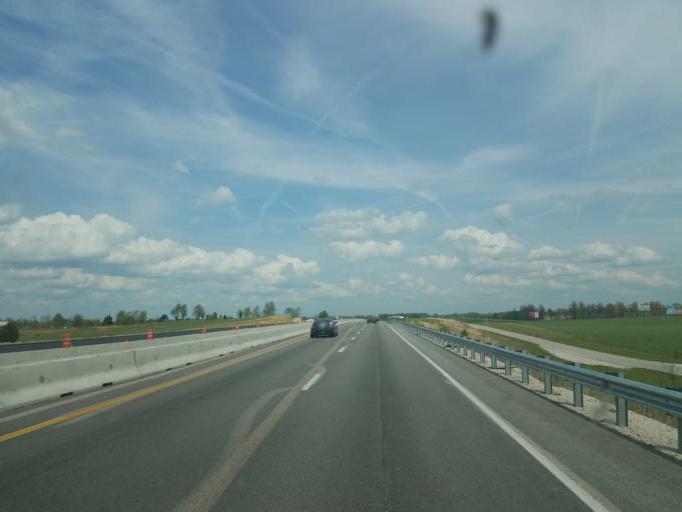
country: US
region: Kentucky
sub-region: Larue County
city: Hodgenville
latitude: 37.4844
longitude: -85.8808
